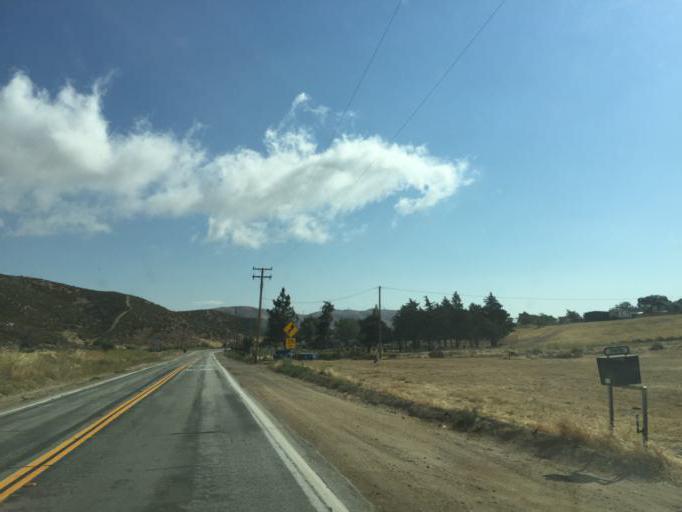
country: US
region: California
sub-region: Los Angeles County
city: Leona Valley
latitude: 34.5926
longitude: -118.2774
